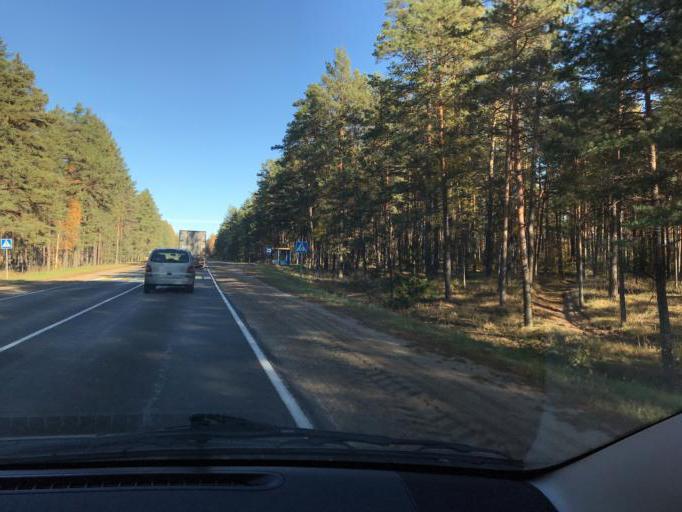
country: BY
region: Vitebsk
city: Polatsk
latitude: 55.3463
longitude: 28.7974
